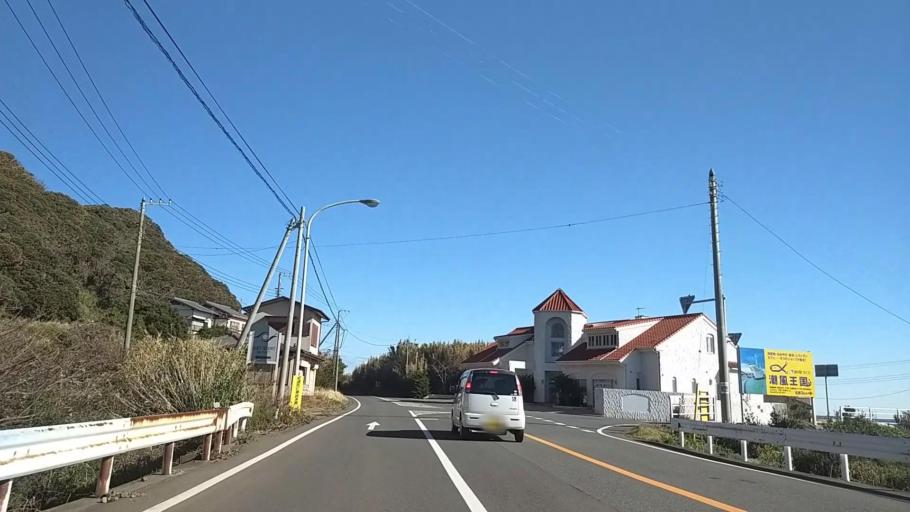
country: JP
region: Chiba
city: Tateyama
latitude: 34.9145
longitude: 139.9308
